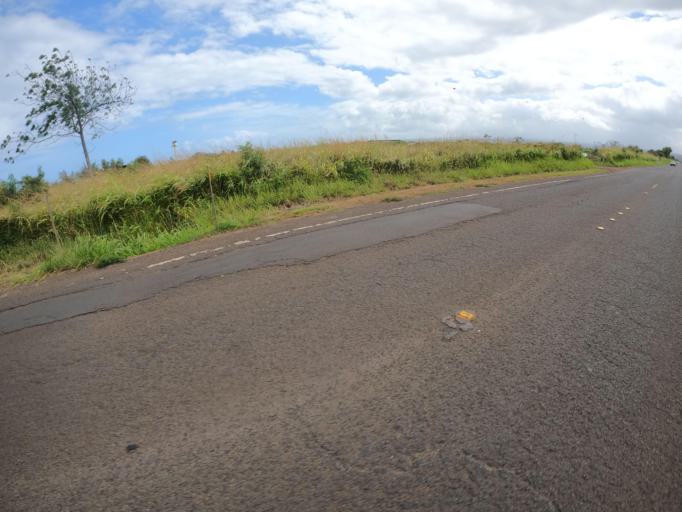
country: US
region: Hawaii
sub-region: Honolulu County
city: Mokuleia
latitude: 21.5730
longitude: -158.1501
